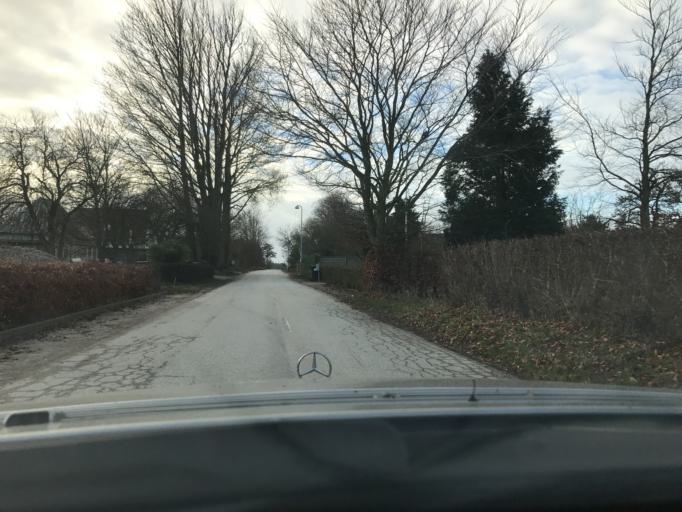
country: DK
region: South Denmark
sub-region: Sonderborg Kommune
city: Nordborg
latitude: 55.0503
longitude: 9.6843
